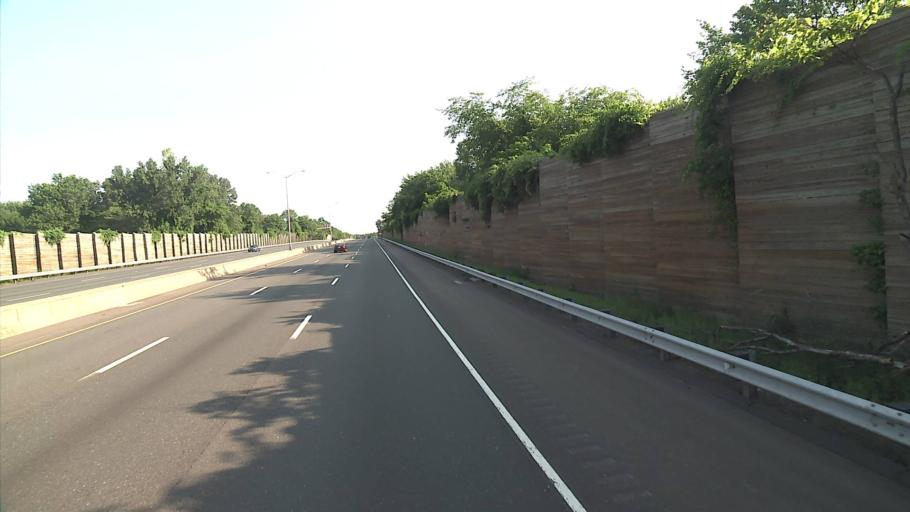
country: US
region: Connecticut
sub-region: Hartford County
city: Thompsonville
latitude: 42.0111
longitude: -72.5859
